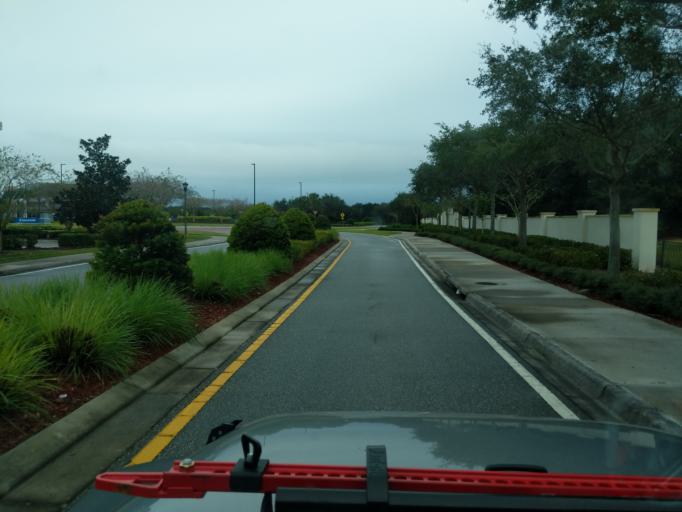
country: US
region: Florida
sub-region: Orange County
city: Winter Garden
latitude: 28.5251
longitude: -81.5866
